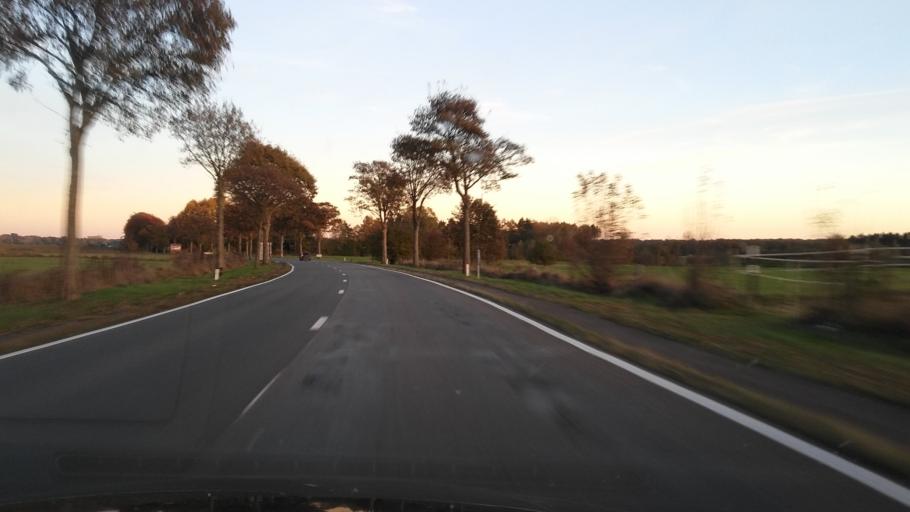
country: BE
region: Wallonia
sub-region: Province du Luxembourg
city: Florenville
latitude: 49.6943
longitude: 5.3241
